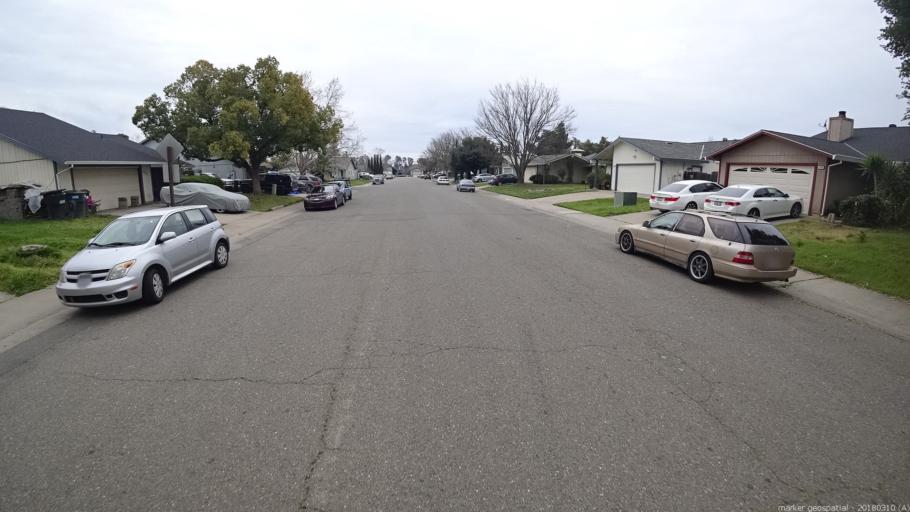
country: US
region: California
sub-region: Sacramento County
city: Florin
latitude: 38.4767
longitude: -121.3862
